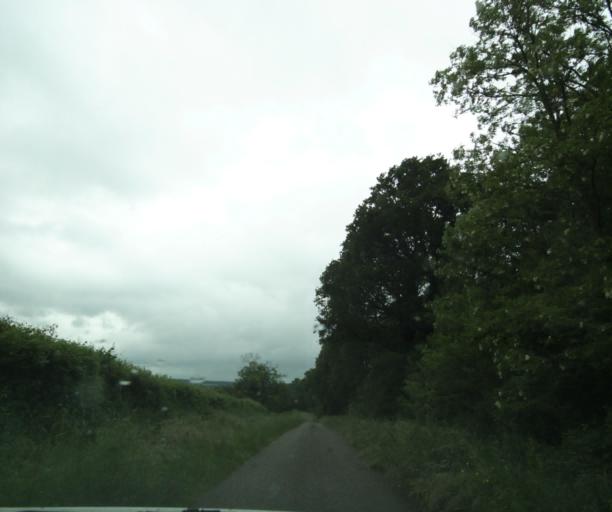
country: FR
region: Bourgogne
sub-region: Departement de Saone-et-Loire
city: Charolles
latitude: 46.4924
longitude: 4.2682
